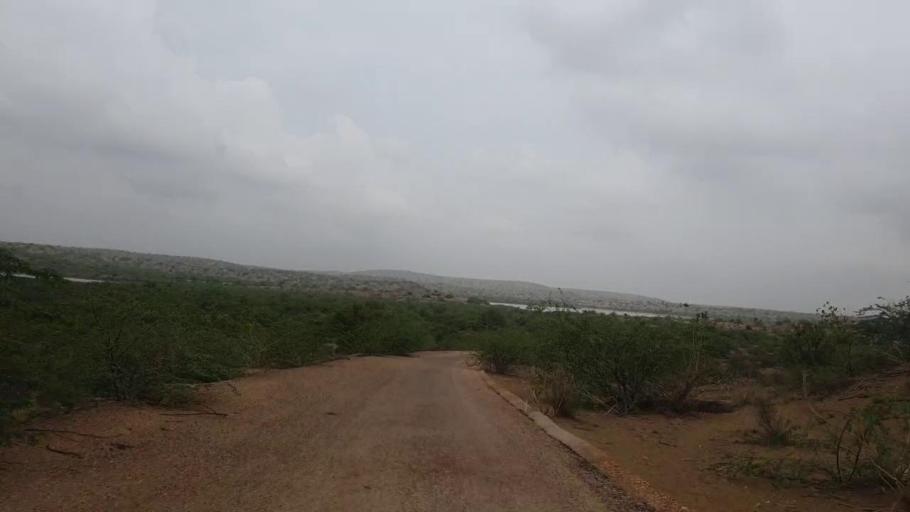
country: PK
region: Sindh
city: Diplo
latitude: 24.5153
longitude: 69.4735
